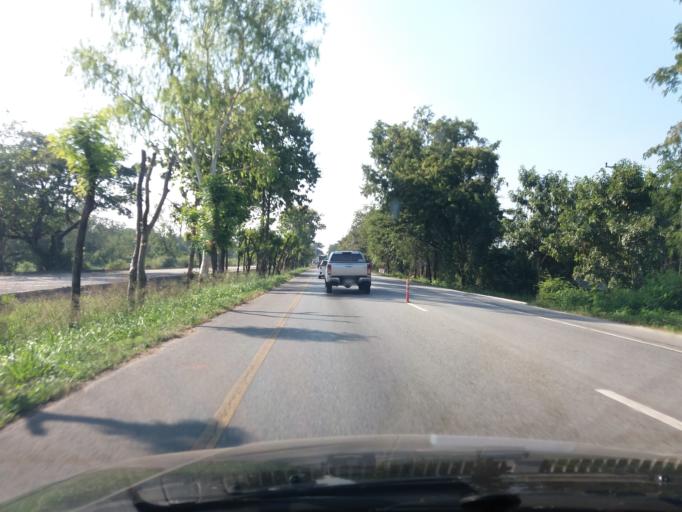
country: TH
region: Nakhon Sawan
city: Nakhon Sawan
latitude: 15.7384
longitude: 100.0193
